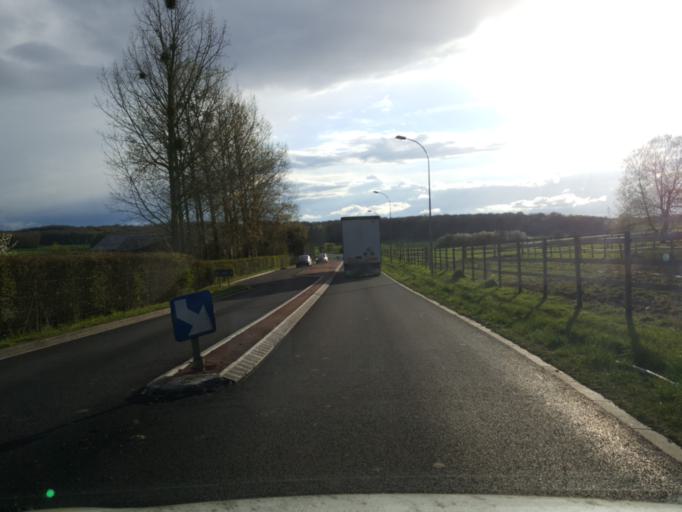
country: FR
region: Ile-de-France
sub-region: Departement des Yvelines
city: Follainville-Dennemont
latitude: 49.0543
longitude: 1.7648
